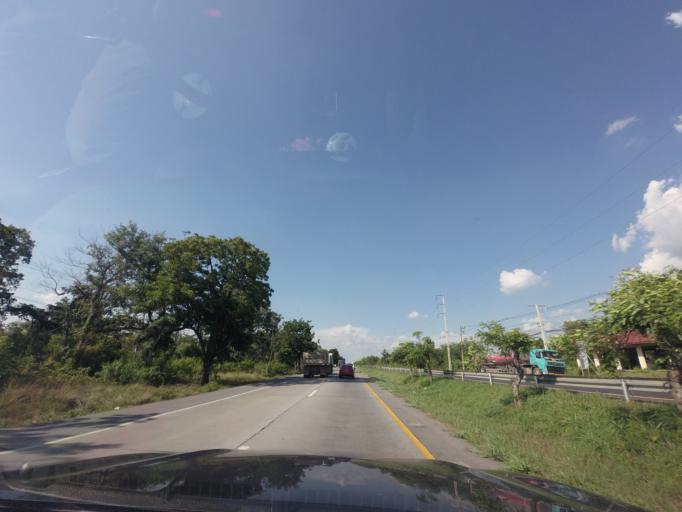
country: TH
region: Nakhon Ratchasima
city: Sida
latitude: 15.5588
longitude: 102.5508
